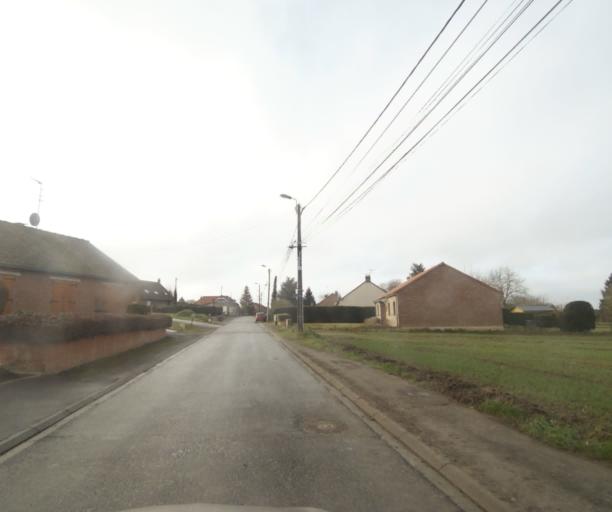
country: FR
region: Nord-Pas-de-Calais
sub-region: Departement du Nord
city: Maing
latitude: 50.3018
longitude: 3.4786
